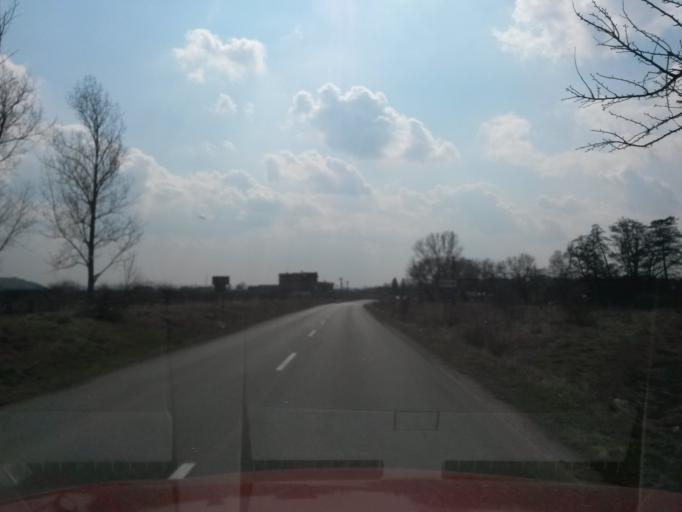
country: SK
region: Kosicky
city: Kosice
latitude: 48.6032
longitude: 21.1719
